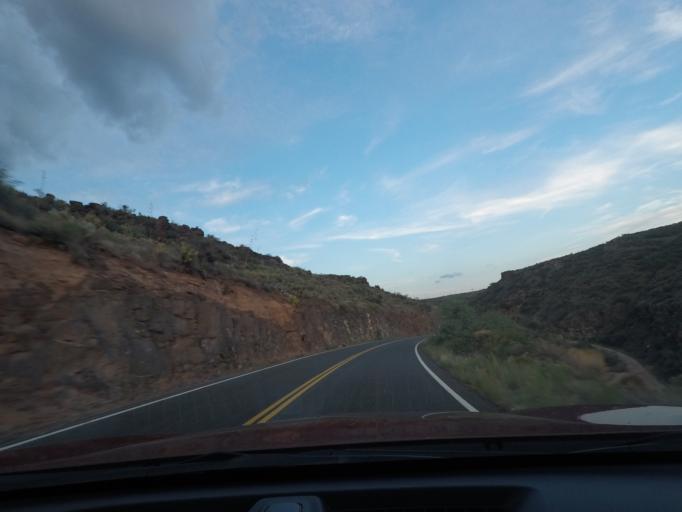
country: US
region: Arizona
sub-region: Yavapai County
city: Congress
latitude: 34.4723
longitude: -112.8155
